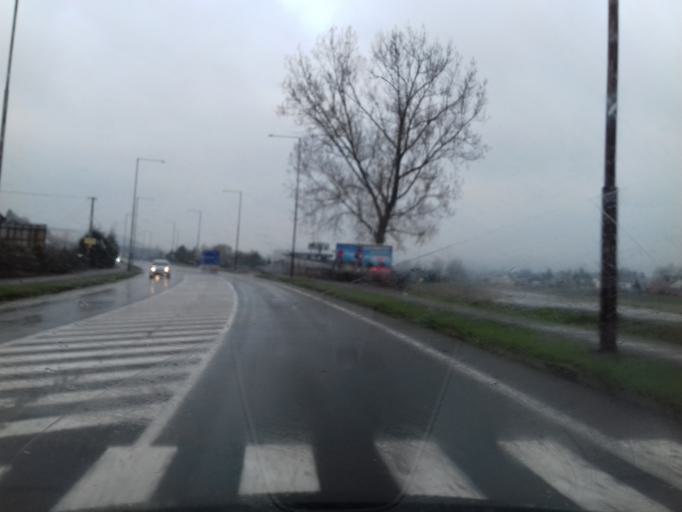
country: SK
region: Presovsky
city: Stara L'ubovna
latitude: 49.3066
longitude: 20.6964
